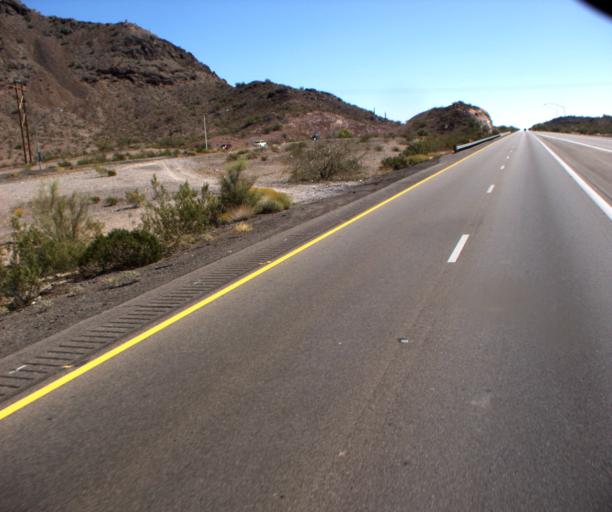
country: US
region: Arizona
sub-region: La Paz County
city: Salome
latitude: 33.6121
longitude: -113.6422
